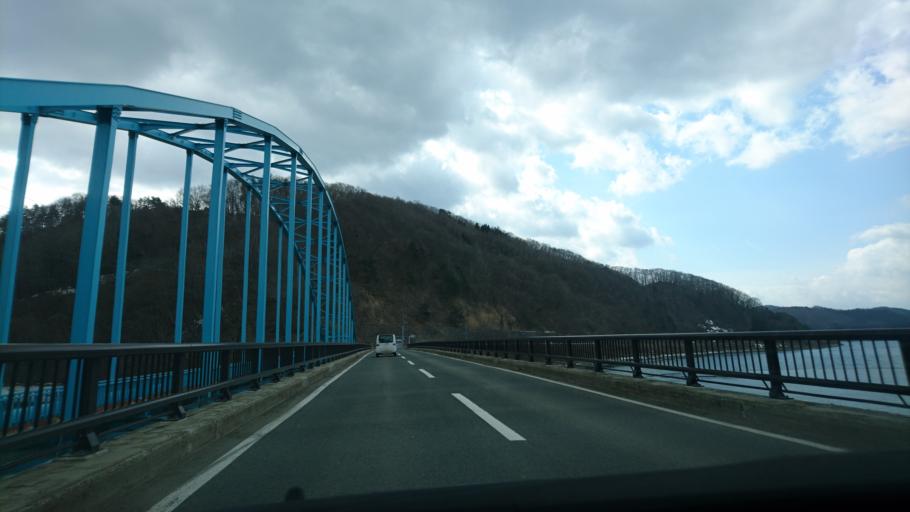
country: JP
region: Iwate
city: Shizukuishi
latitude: 39.6884
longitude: 141.0332
